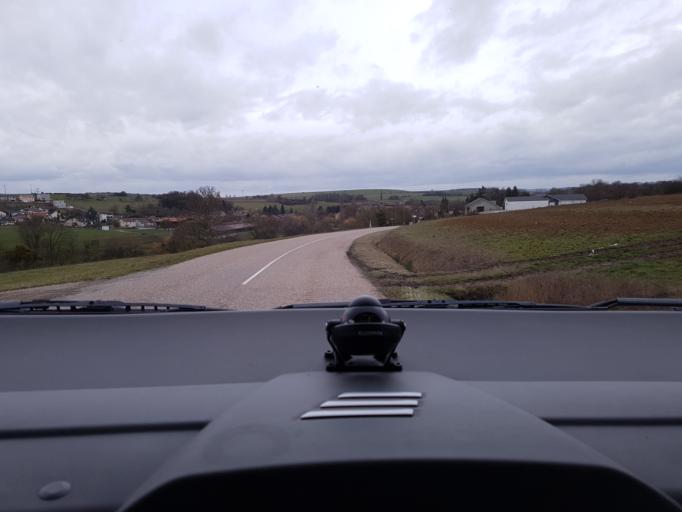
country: FR
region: Lorraine
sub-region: Departement de la Moselle
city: Crehange
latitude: 49.0574
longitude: 6.5564
